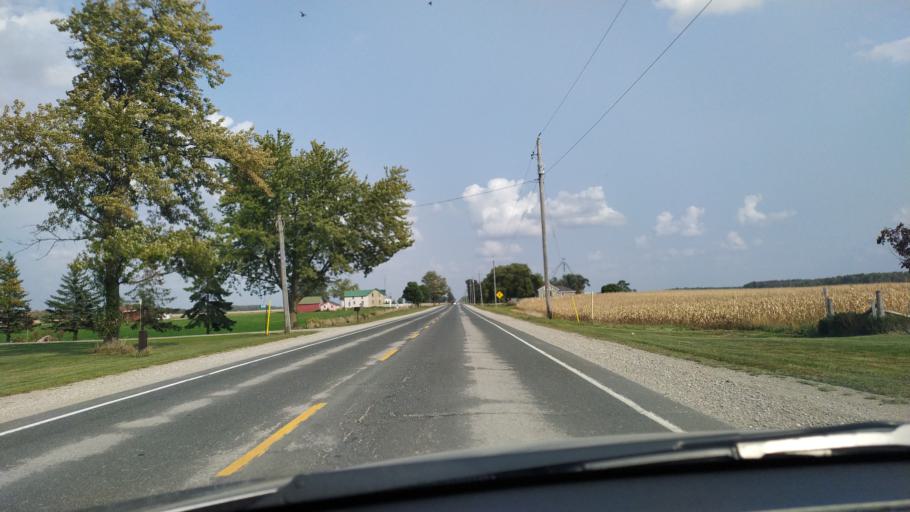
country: CA
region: Ontario
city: Stratford
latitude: 43.3514
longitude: -80.8660
